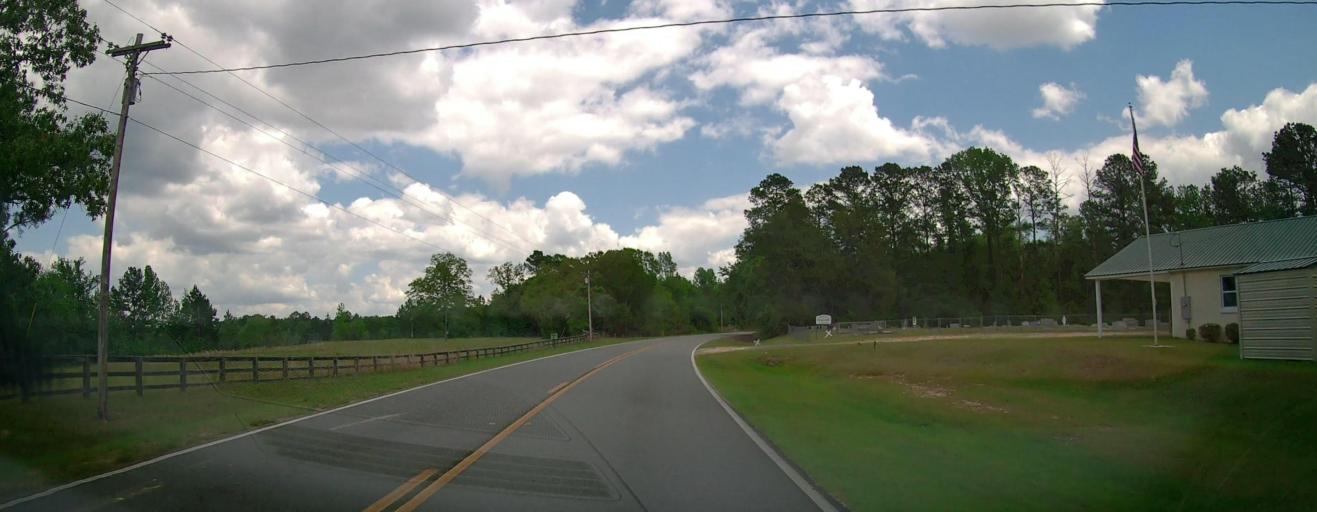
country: US
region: Georgia
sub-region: Laurens County
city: East Dublin
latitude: 32.5251
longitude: -82.7567
